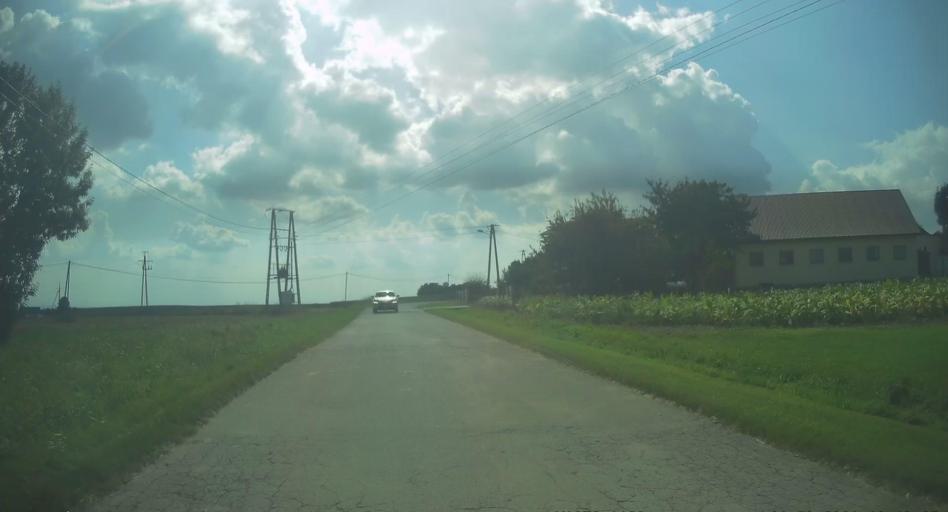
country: PL
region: Lesser Poland Voivodeship
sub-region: Powiat proszowicki
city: Nowe Brzesko
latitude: 50.1576
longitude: 20.4502
